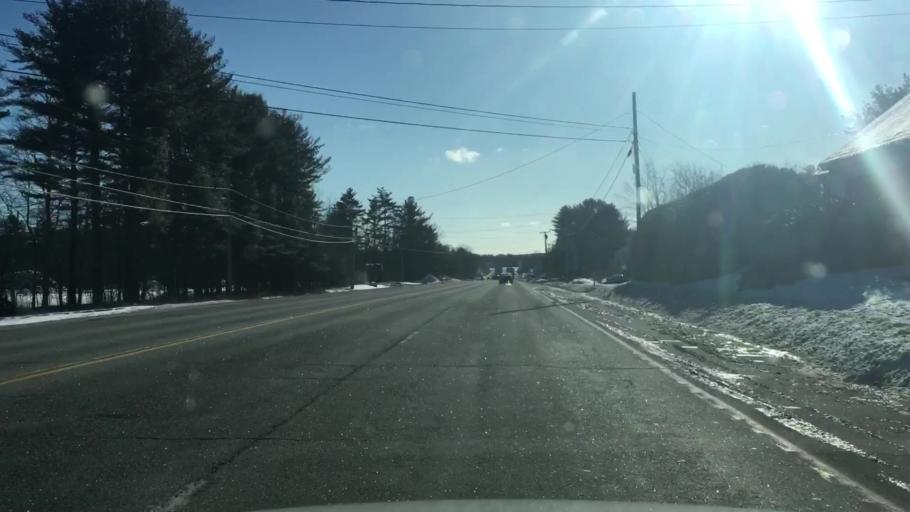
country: US
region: Maine
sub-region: Androscoggin County
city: Lewiston
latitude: 44.1702
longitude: -70.2326
